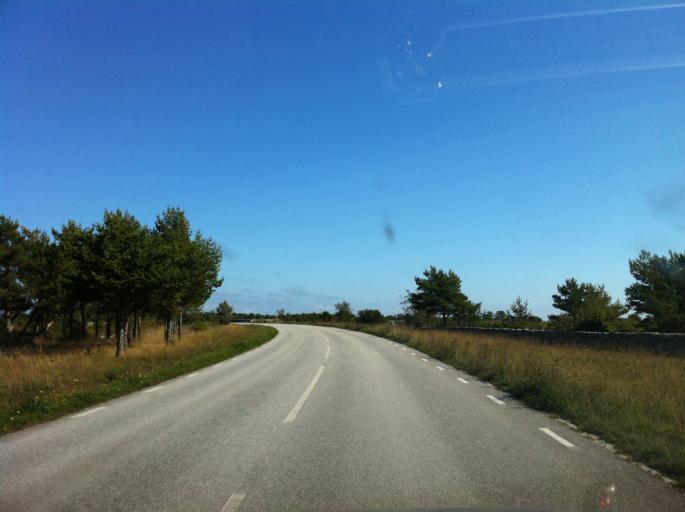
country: SE
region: Gotland
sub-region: Gotland
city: Slite
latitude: 57.9345
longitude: 19.1848
